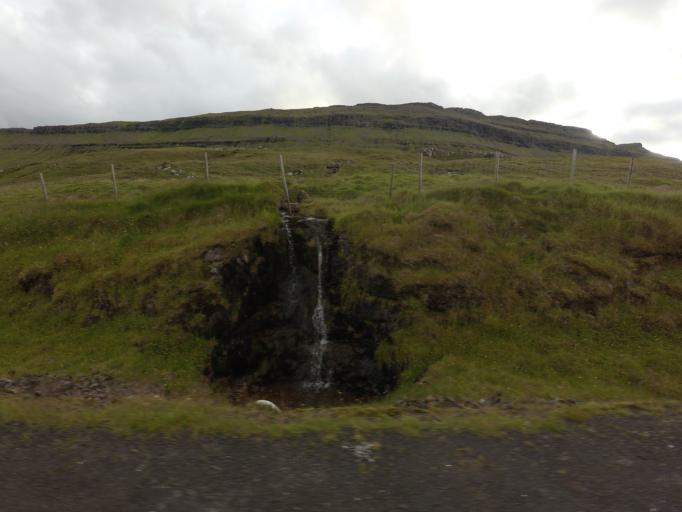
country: FO
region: Streymoy
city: Kollafjordhur
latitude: 62.1373
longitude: -6.8873
